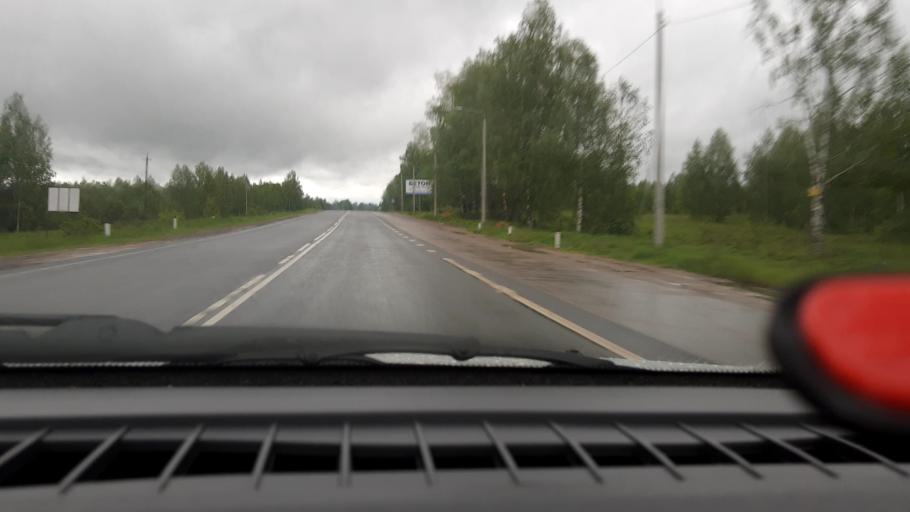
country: RU
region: Nizjnij Novgorod
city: Semenov
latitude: 56.8226
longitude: 44.5826
